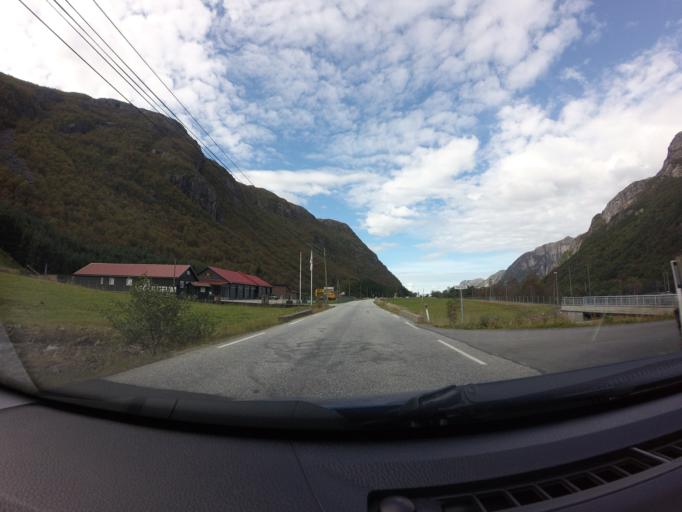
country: NO
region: Rogaland
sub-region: Forsand
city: Forsand
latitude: 58.8214
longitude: 6.2011
